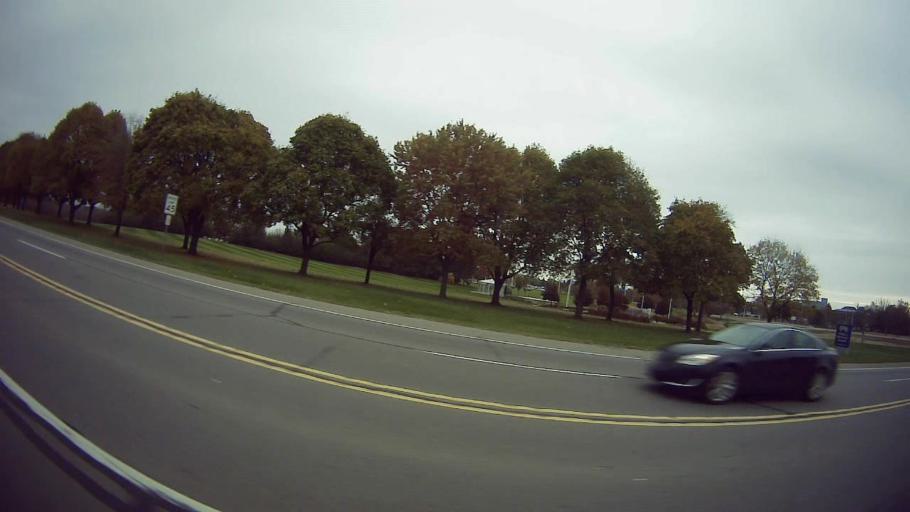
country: US
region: Michigan
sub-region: Oakland County
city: Pontiac
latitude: 42.6601
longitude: -83.3351
